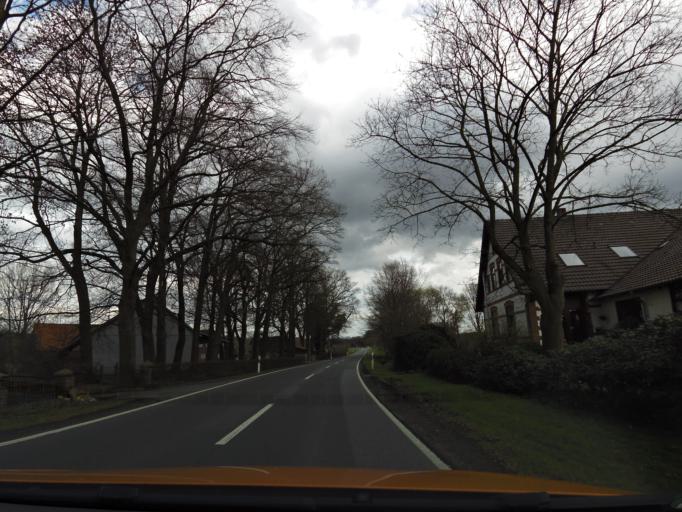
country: DE
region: Lower Saxony
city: Bassum
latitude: 52.8895
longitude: 8.7033
